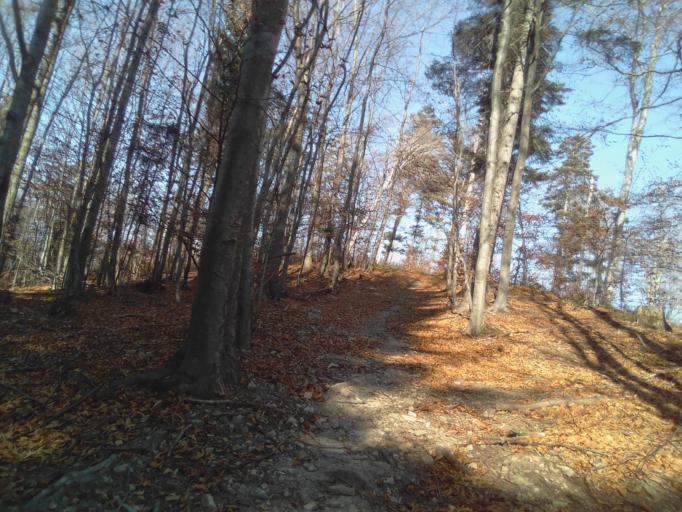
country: PL
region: Subcarpathian Voivodeship
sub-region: Powiat krosnienski
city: Leki
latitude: 49.8338
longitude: 21.6846
